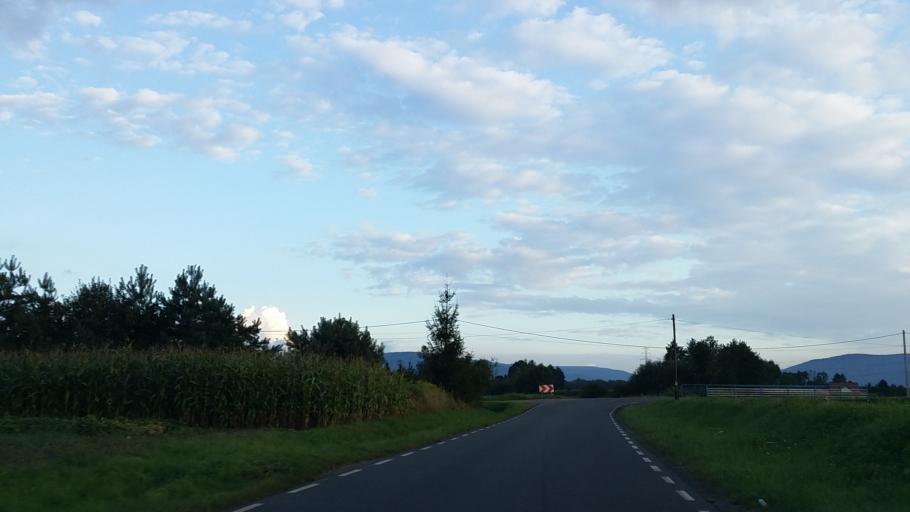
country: PL
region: Lesser Poland Voivodeship
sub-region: Powiat oswiecimski
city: Nowa Wies
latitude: 49.9094
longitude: 19.2296
